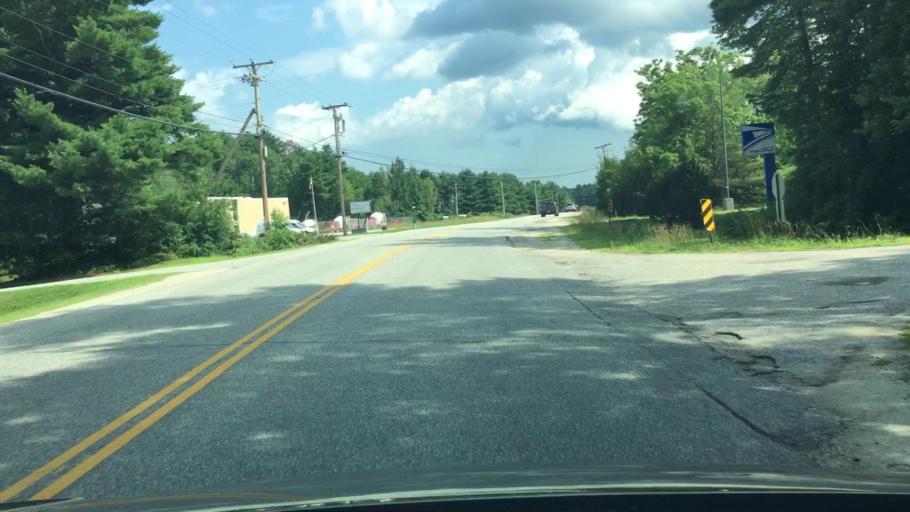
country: US
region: Maine
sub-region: Androscoggin County
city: Auburn
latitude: 44.0762
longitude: -70.2572
